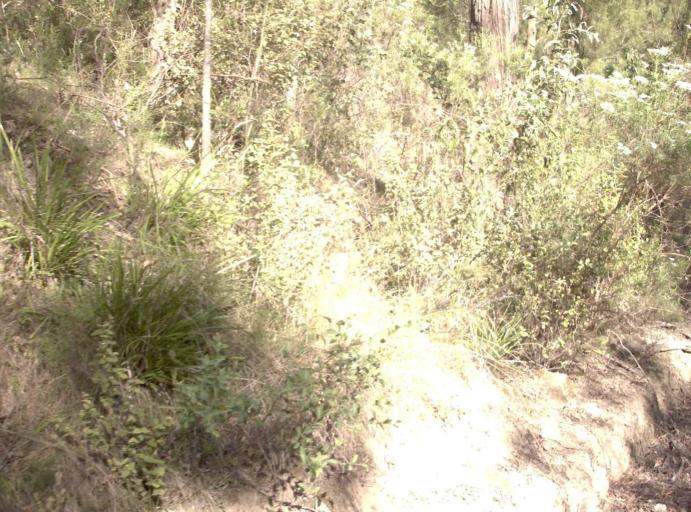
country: AU
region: Victoria
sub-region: East Gippsland
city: Lakes Entrance
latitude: -37.4800
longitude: 148.5562
